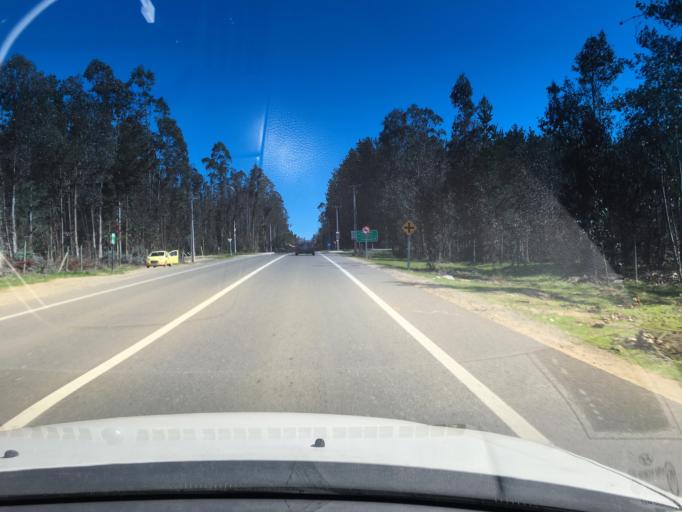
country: CL
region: Valparaiso
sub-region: San Antonio Province
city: El Tabo
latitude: -33.4270
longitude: -71.6387
